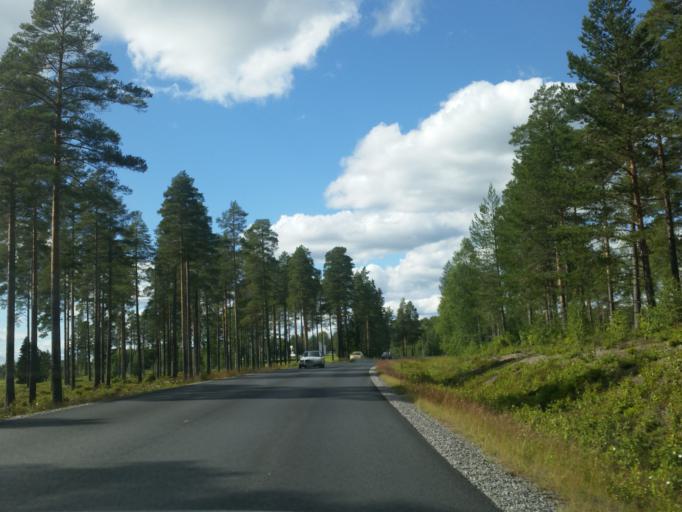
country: SE
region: Vaesterbotten
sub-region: Robertsfors Kommun
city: Robertsfors
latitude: 64.1846
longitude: 20.8689
